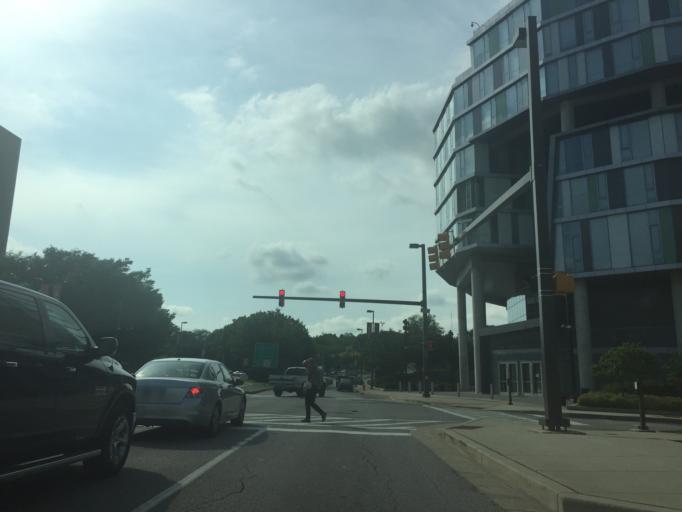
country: US
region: Maryland
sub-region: City of Baltimore
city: Baltimore
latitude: 39.3099
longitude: -76.6235
